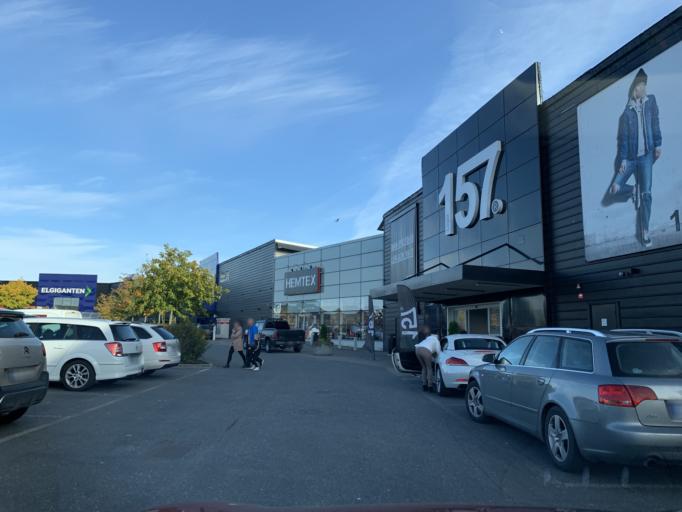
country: SE
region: Stockholm
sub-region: Haninge Kommun
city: Handen
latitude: 59.1974
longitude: 18.1272
